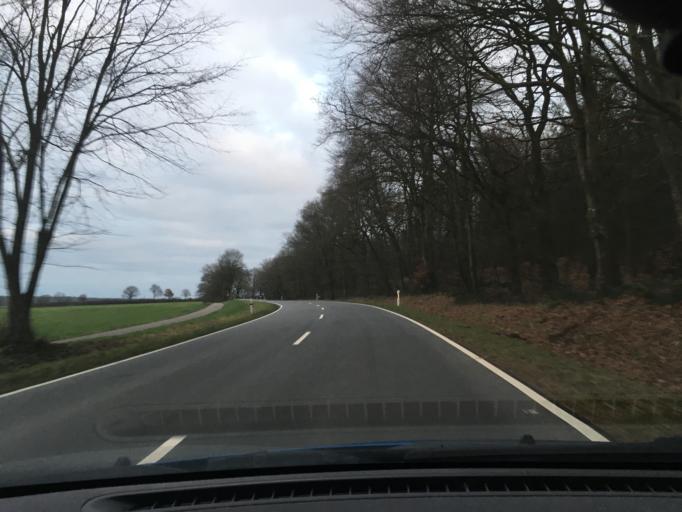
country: DE
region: Schleswig-Holstein
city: Mehlbek
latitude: 53.9962
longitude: 9.4468
